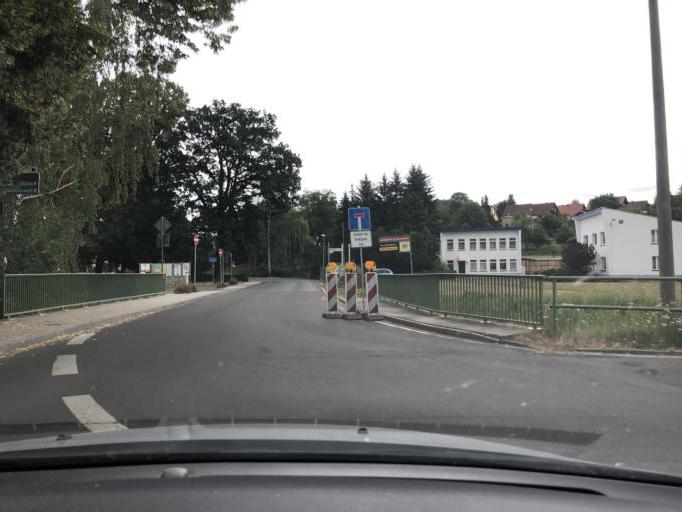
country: DE
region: Thuringia
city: Langenleuba-Niederhain
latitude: 51.0171
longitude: 12.5998
